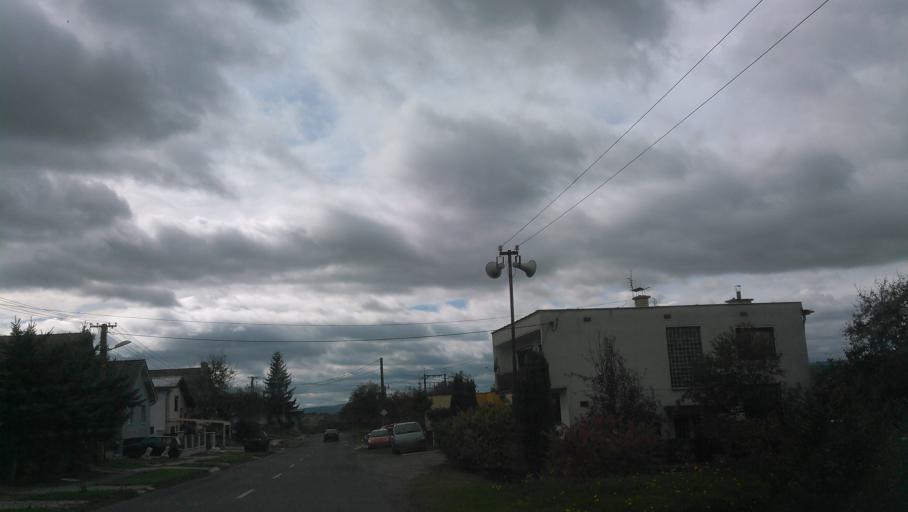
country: SK
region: Banskobystricky
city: Lucenec
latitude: 48.3949
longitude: 19.7032
